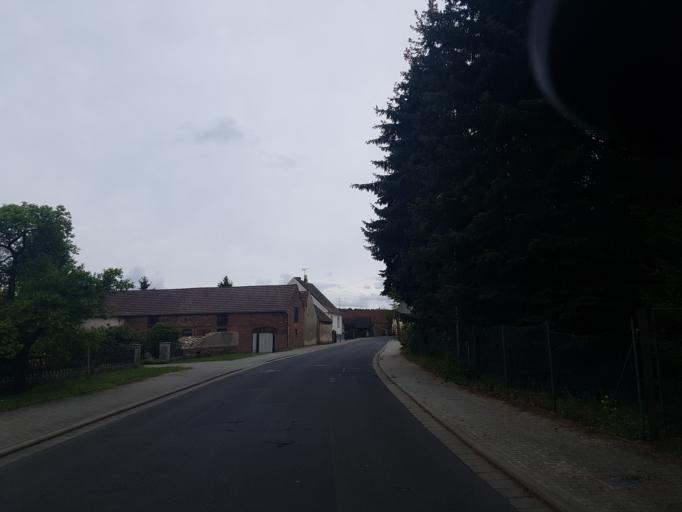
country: DE
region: Brandenburg
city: Tschernitz
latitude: 51.6217
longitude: 14.6007
